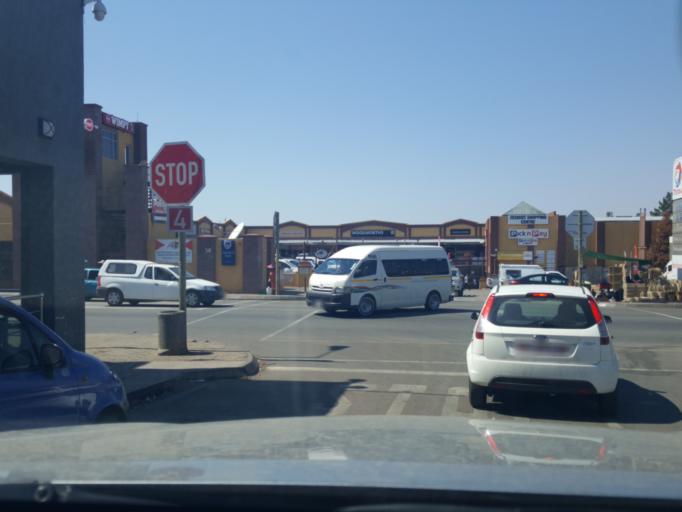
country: ZA
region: North-West
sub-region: Ngaka Modiri Molema District Municipality
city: Zeerust
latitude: -25.5440
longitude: 26.0829
